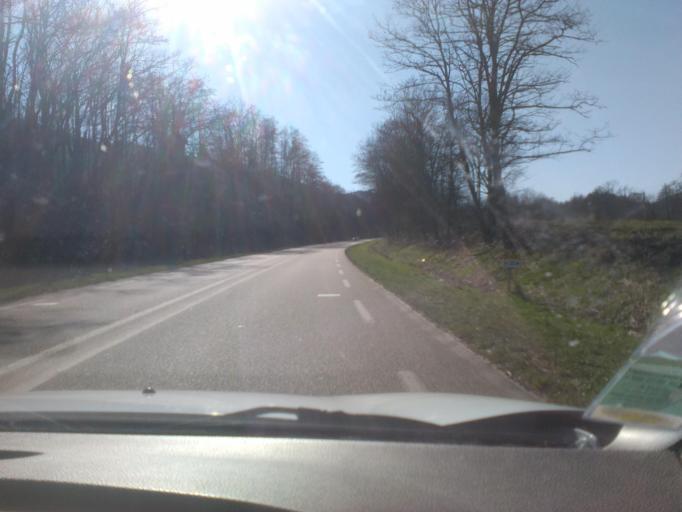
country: FR
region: Alsace
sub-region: Departement du Bas-Rhin
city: Lutzelhouse
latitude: 48.5080
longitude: 7.2830
